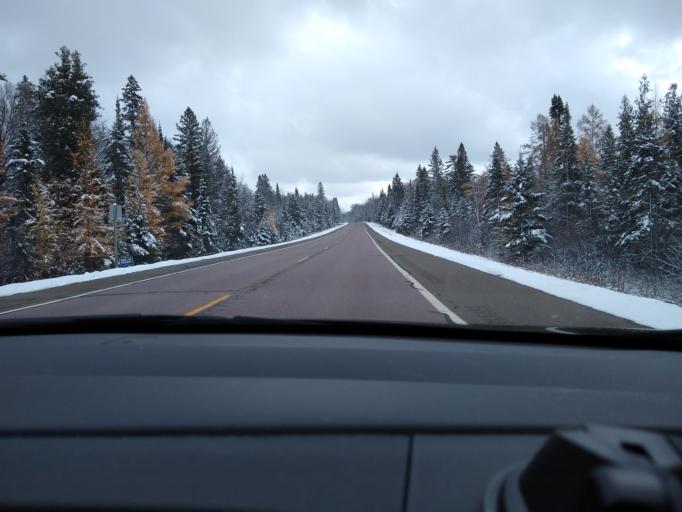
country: US
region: Michigan
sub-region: Iron County
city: Iron River
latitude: 46.1754
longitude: -88.9490
